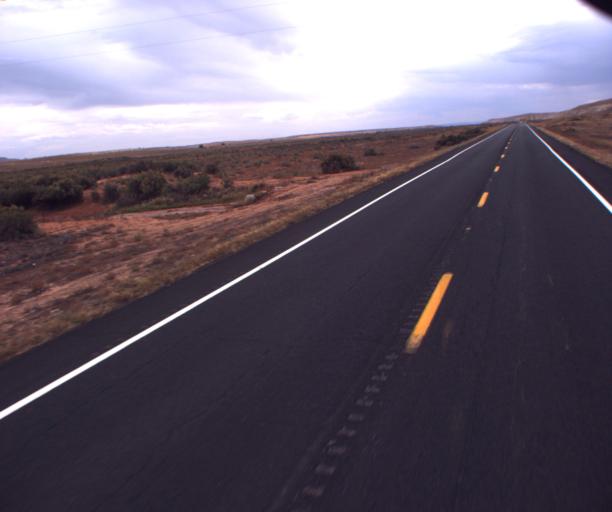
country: US
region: Arizona
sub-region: Coconino County
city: Kaibito
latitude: 36.3507
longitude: -110.9100
